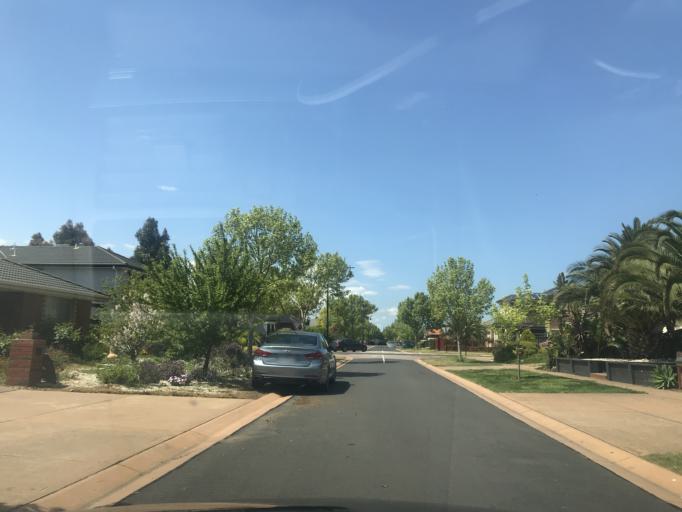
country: AU
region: Victoria
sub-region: Wyndham
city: Hoppers Crossing
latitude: -37.8877
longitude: 144.7284
